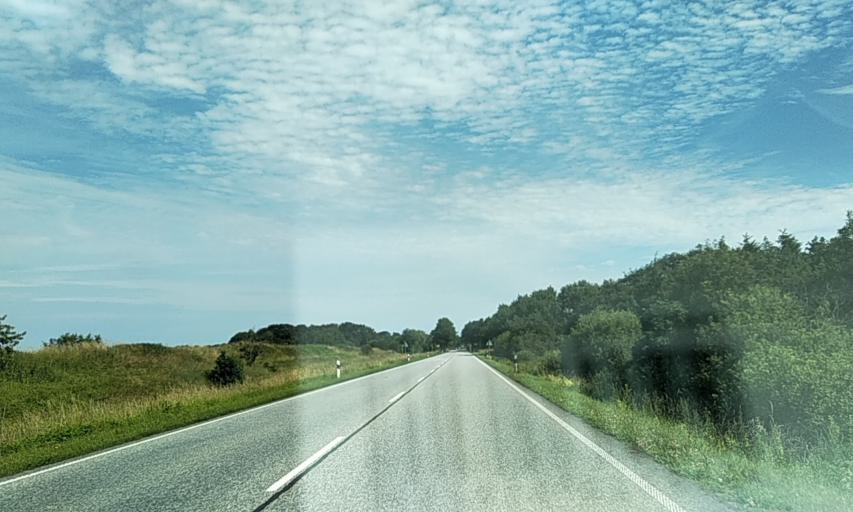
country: DE
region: Schleswig-Holstein
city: Jagel
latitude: 54.4494
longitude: 9.5373
